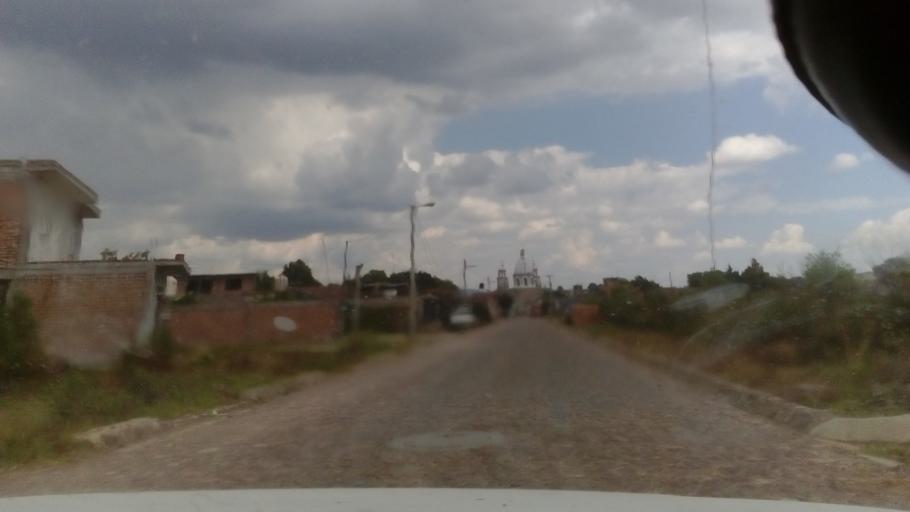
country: MX
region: Guanajuato
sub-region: Silao de la Victoria
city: San Francisco (Banos de Agua Caliente)
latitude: 21.2086
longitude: -101.4275
